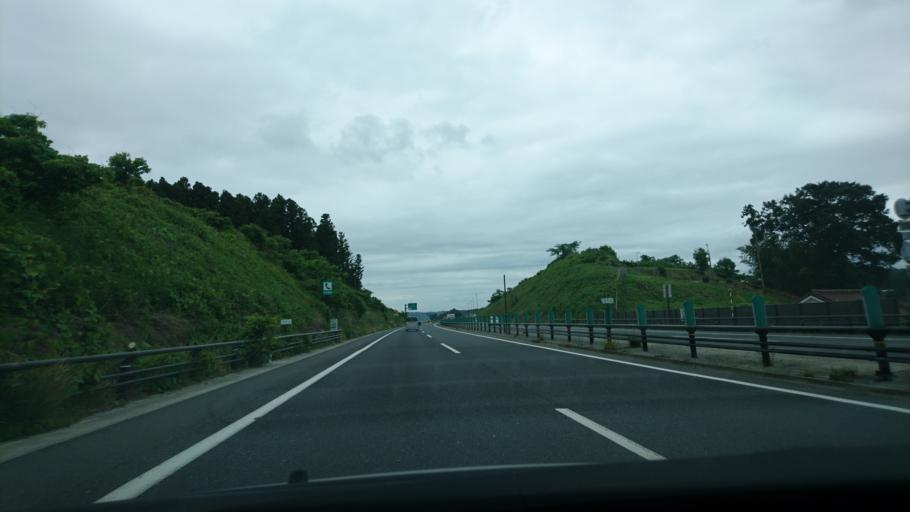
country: JP
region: Miyagi
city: Wakuya
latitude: 38.5568
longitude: 141.2702
